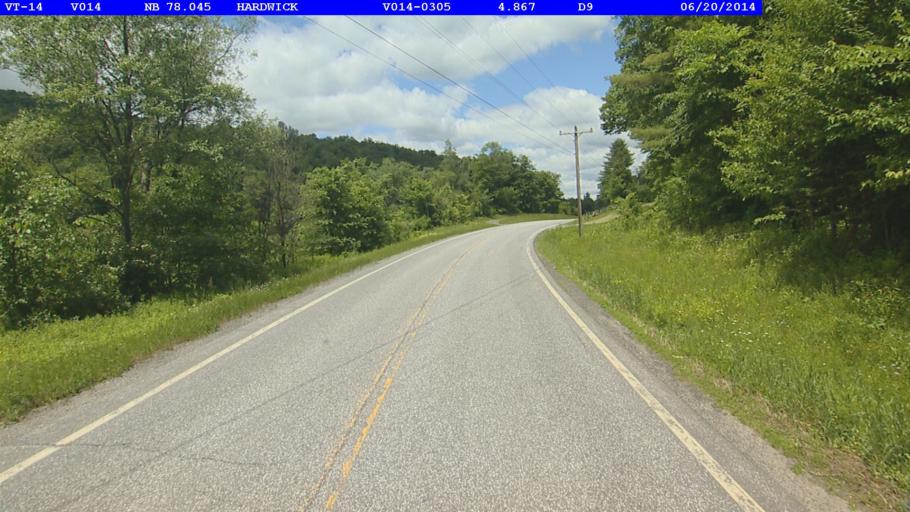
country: US
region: Vermont
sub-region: Caledonia County
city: Hardwick
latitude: 44.5636
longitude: -72.3676
